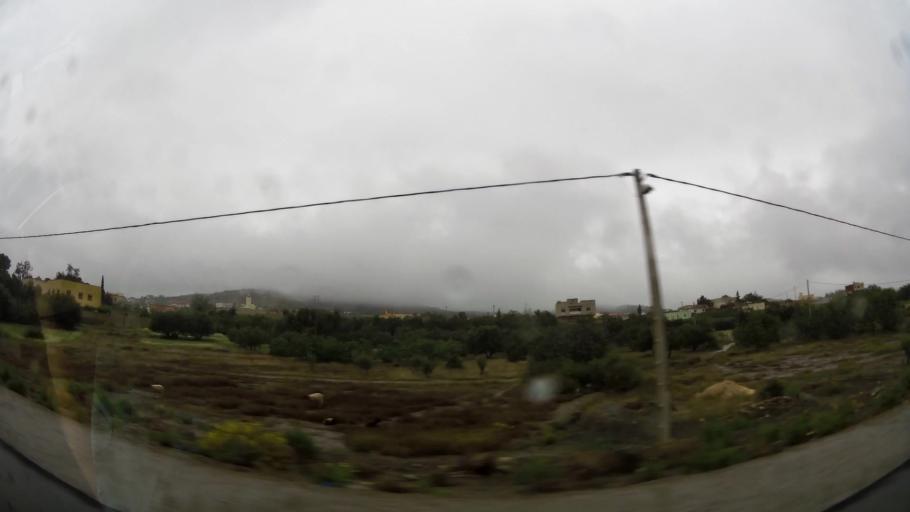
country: MA
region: Taza-Al Hoceima-Taounate
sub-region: Taza
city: Aknoul
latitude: 34.8117
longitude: -3.7344
